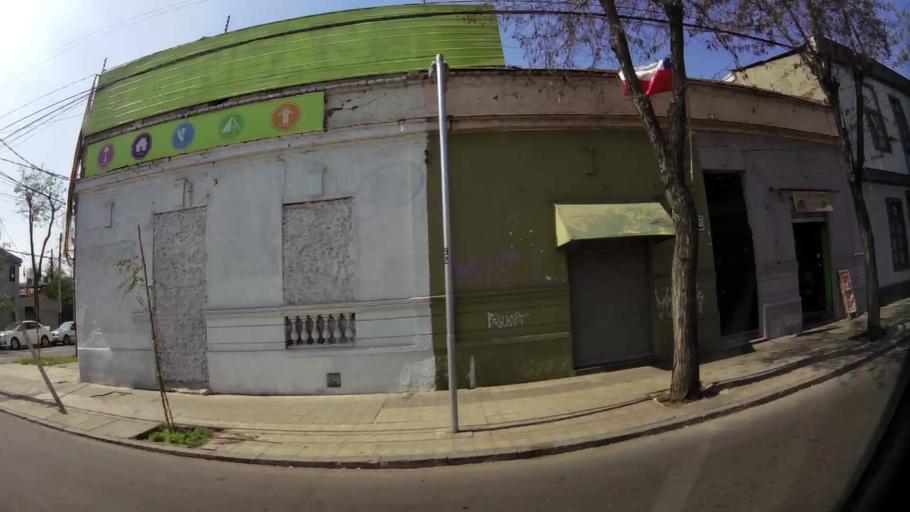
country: CL
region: Santiago Metropolitan
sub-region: Provincia de Santiago
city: Santiago
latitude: -33.4652
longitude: -70.6733
